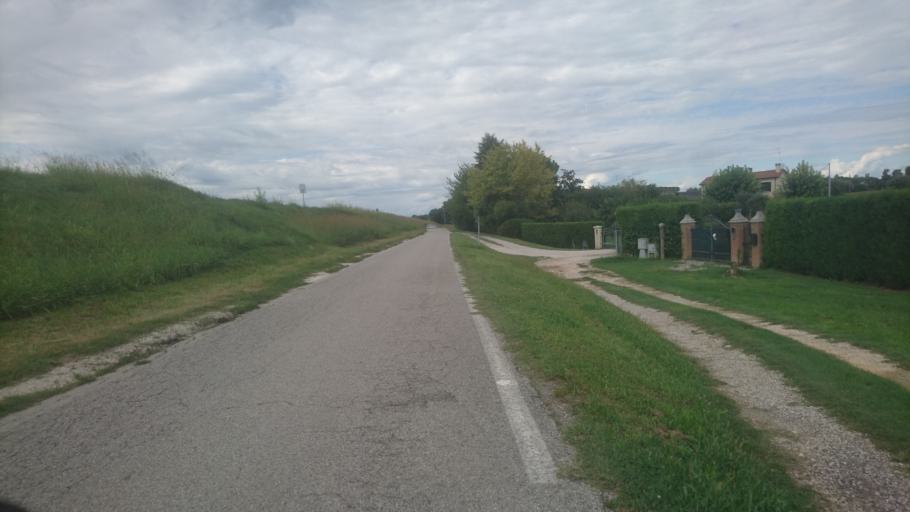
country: IT
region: Veneto
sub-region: Provincia di Padova
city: Oltre Brenta
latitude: 45.4024
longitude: 12.0038
